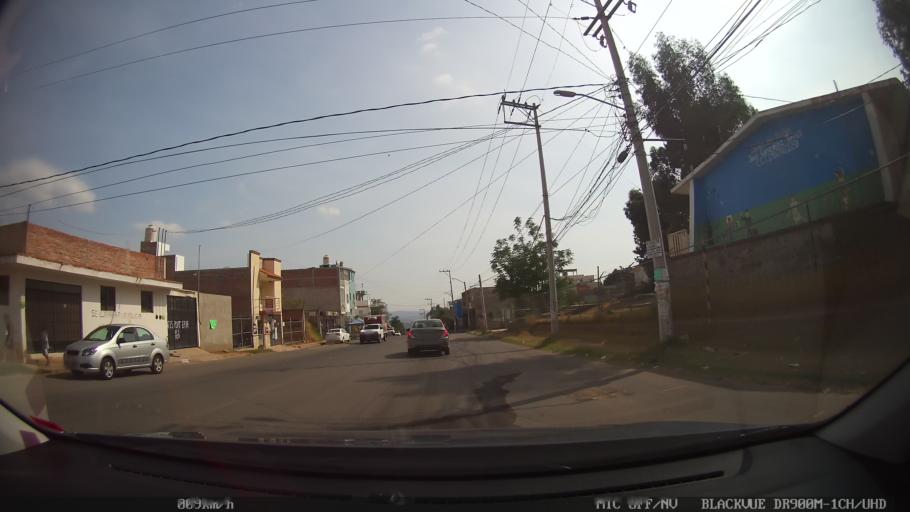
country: MX
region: Jalisco
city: Tonala
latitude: 20.6366
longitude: -103.2356
